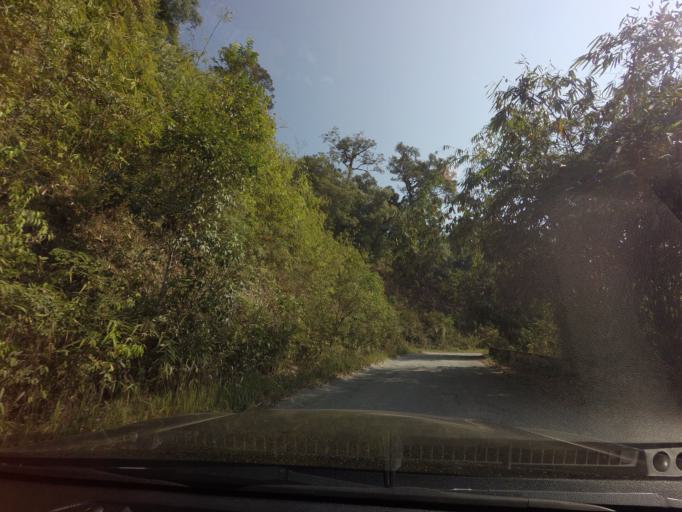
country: TH
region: Kanchanaburi
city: Thong Pha Phum
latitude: 14.6901
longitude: 98.4567
